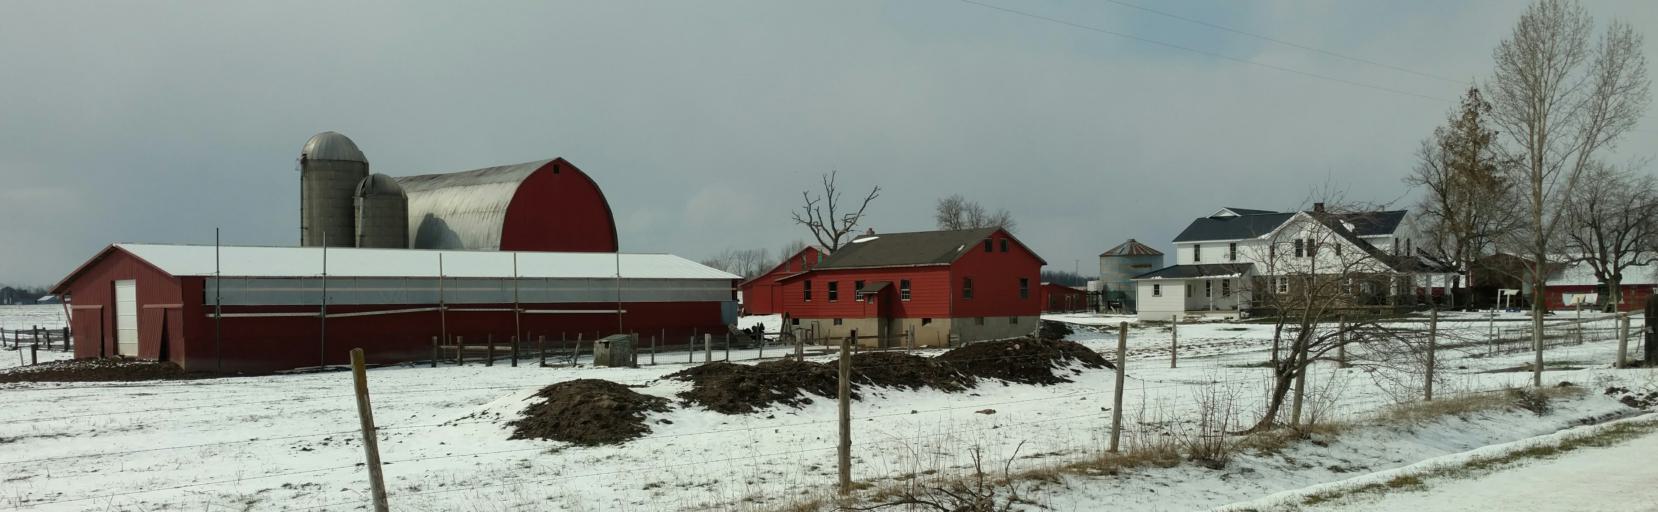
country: US
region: Michigan
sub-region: Gladwin County
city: Gladwin
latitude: 44.0697
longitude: -84.4678
